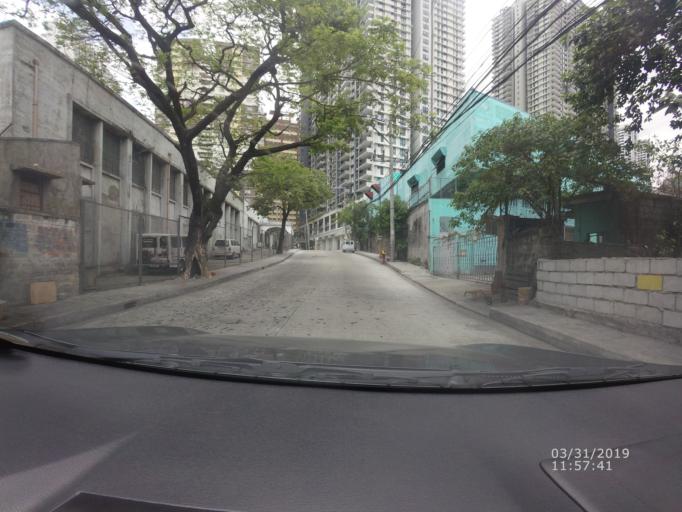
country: PH
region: Metro Manila
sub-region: Mandaluyong
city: Mandaluyong City
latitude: 14.5737
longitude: 121.0515
